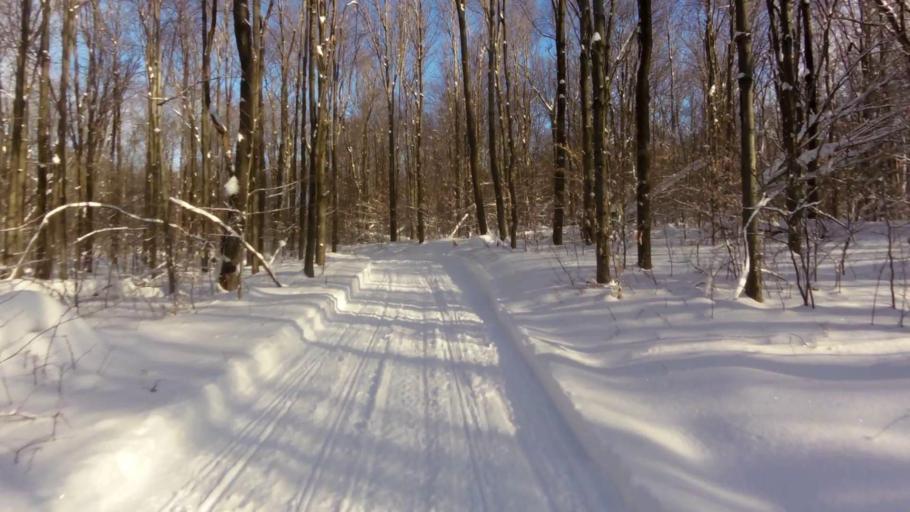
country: US
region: New York
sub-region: Chautauqua County
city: Falconer
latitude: 42.2748
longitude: -79.1282
